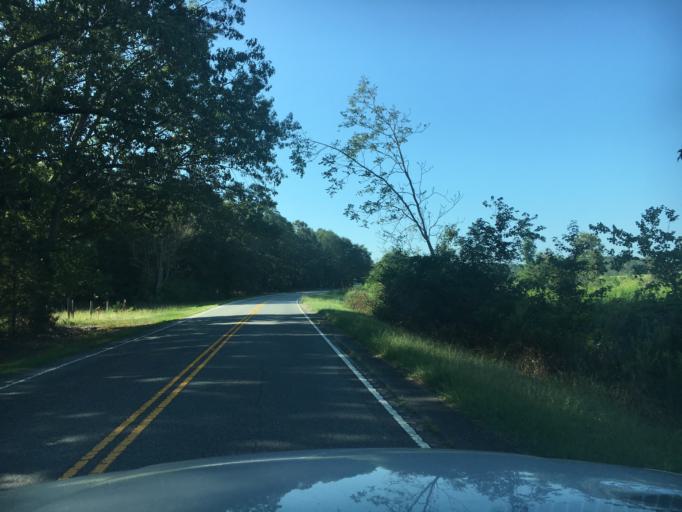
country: US
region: South Carolina
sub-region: Anderson County
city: Williamston
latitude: 34.6303
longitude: -82.3480
